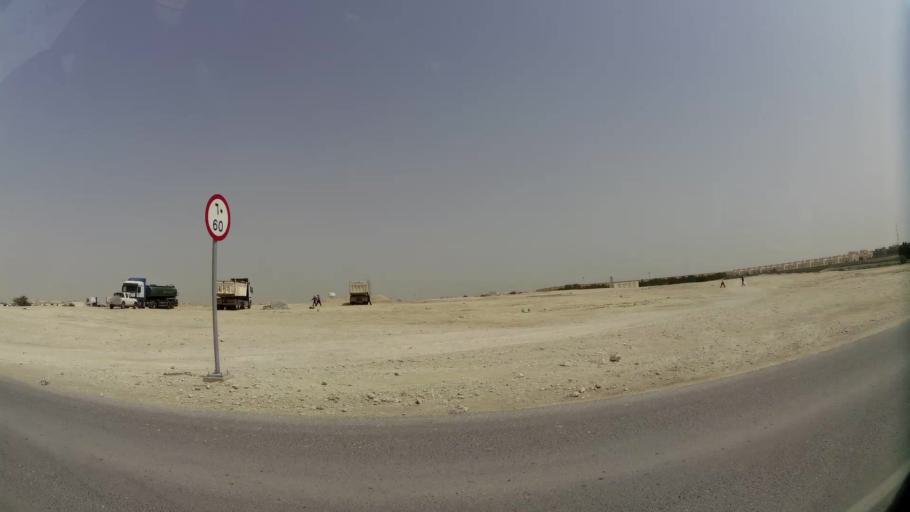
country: QA
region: Baladiyat ar Rayyan
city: Ar Rayyan
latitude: 25.2340
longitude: 51.4064
